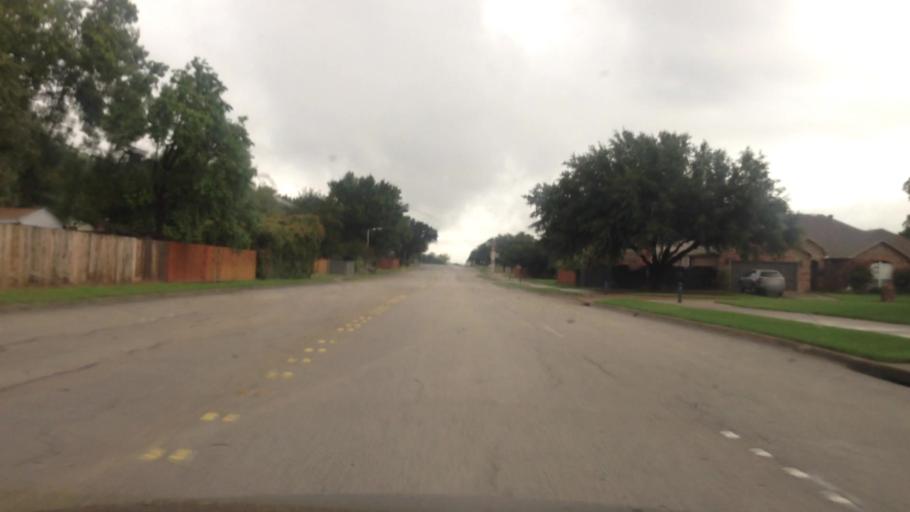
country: US
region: Texas
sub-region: Tarrant County
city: North Richland Hills
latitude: 32.8633
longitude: -97.2033
